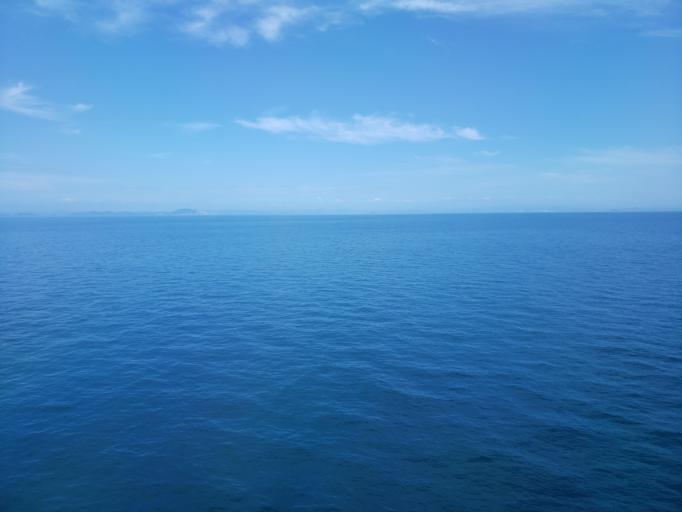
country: JP
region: Hyogo
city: Shirahamacho-usazakiminami
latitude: 34.5365
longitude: 134.6951
